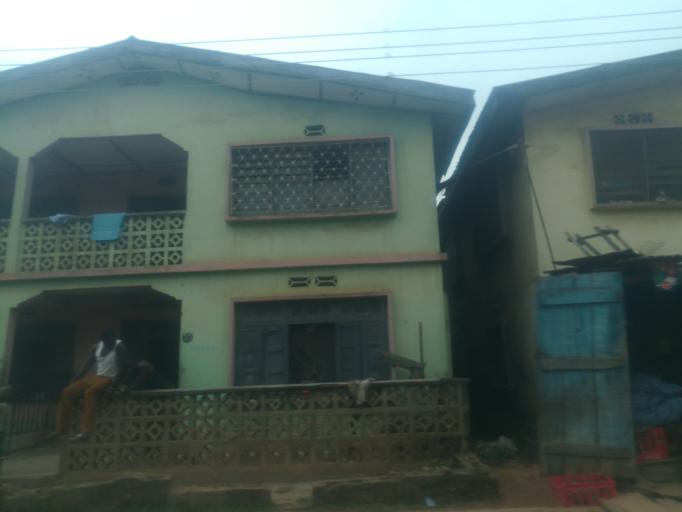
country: NG
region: Oyo
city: Ibadan
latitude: 7.4447
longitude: 3.9122
